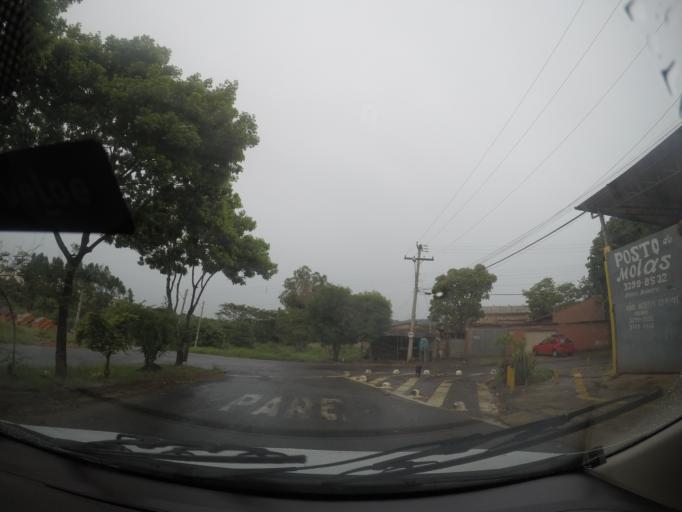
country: BR
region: Goias
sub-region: Goiania
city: Goiania
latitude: -16.6743
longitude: -49.3247
